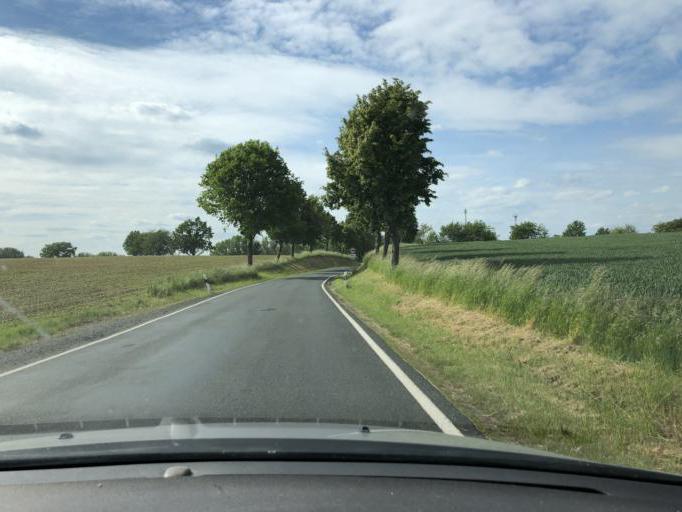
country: DE
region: Saxony
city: Nerchau
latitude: 51.2411
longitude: 12.8164
